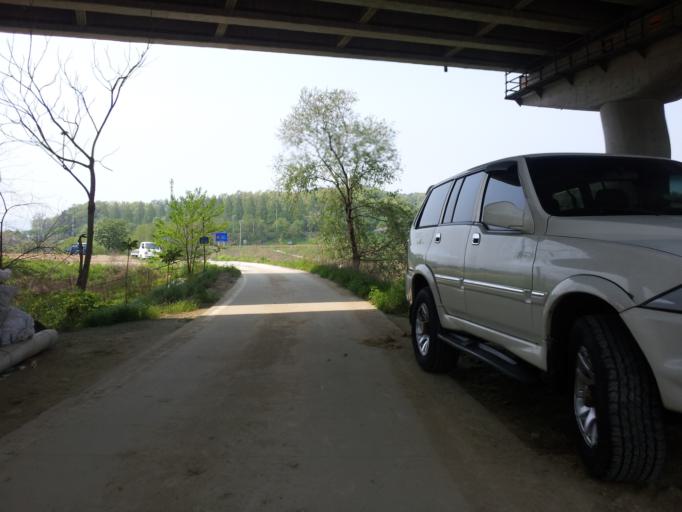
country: KR
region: Daejeon
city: Daejeon
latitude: 36.2650
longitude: 127.2910
